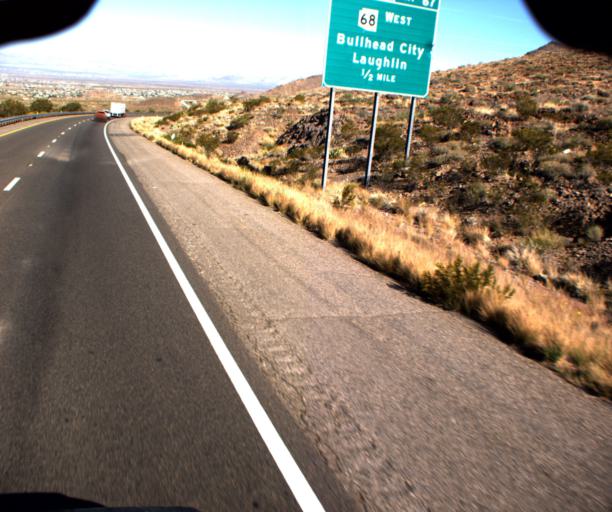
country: US
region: Arizona
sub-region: Mohave County
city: Kingman
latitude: 35.2116
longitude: -114.1099
